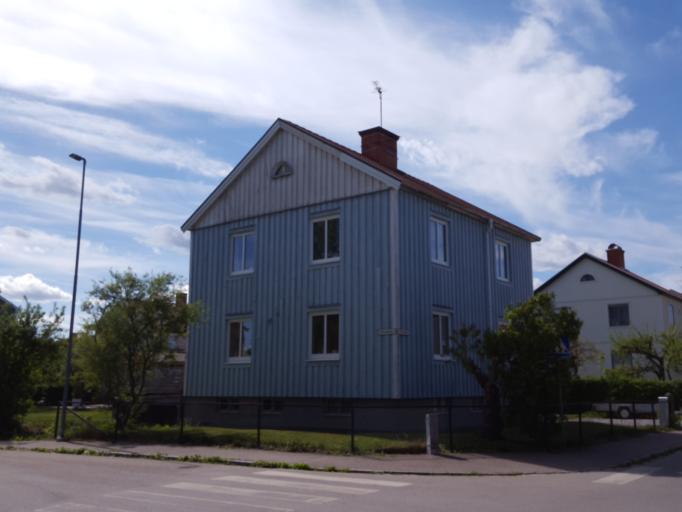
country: SE
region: Uppsala
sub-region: Uppsala Kommun
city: Uppsala
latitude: 59.8593
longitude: 17.6615
